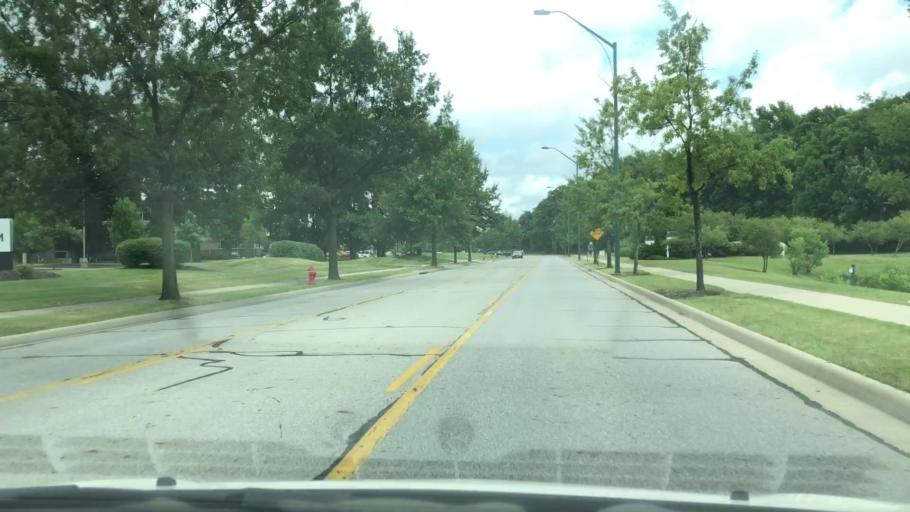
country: US
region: Ohio
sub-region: Franklin County
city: Westerville
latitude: 40.1392
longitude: -82.9211
